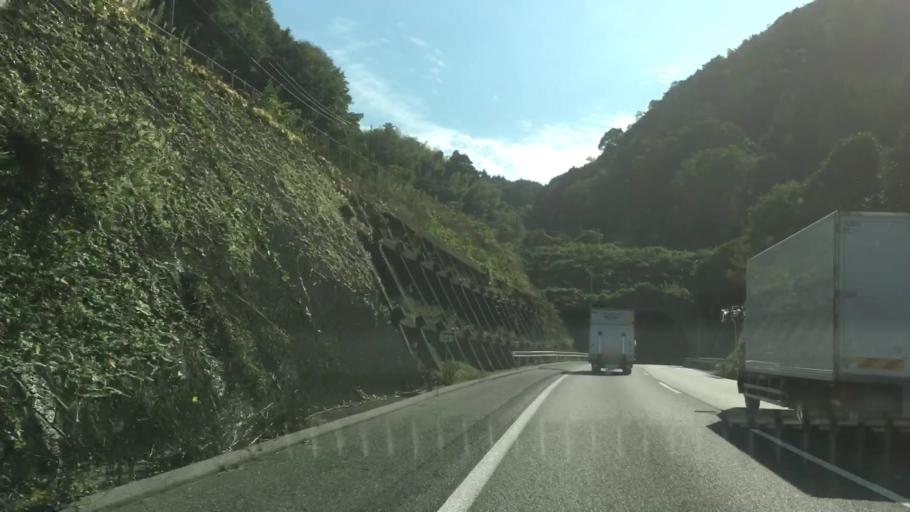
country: JP
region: Yamaguchi
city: Otake
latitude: 34.2315
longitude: 132.2118
